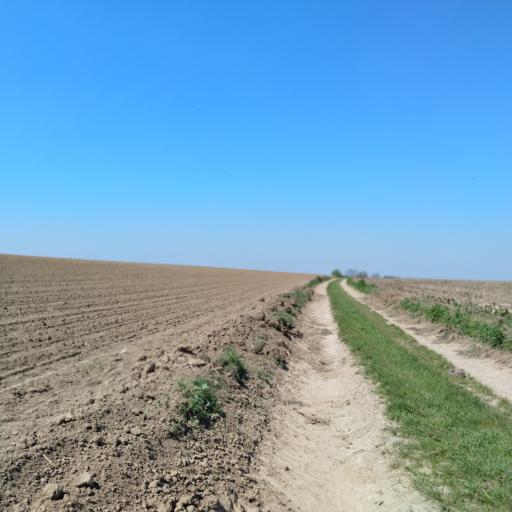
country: BE
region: Wallonia
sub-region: Province du Hainaut
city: Lens
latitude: 50.5748
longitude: 3.8821
